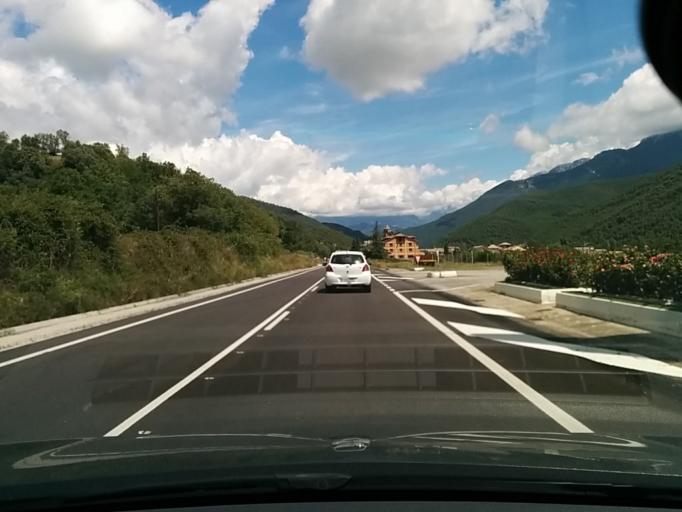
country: ES
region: Aragon
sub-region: Provincia de Huesca
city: Labuerda
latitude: 42.4462
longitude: 0.1324
